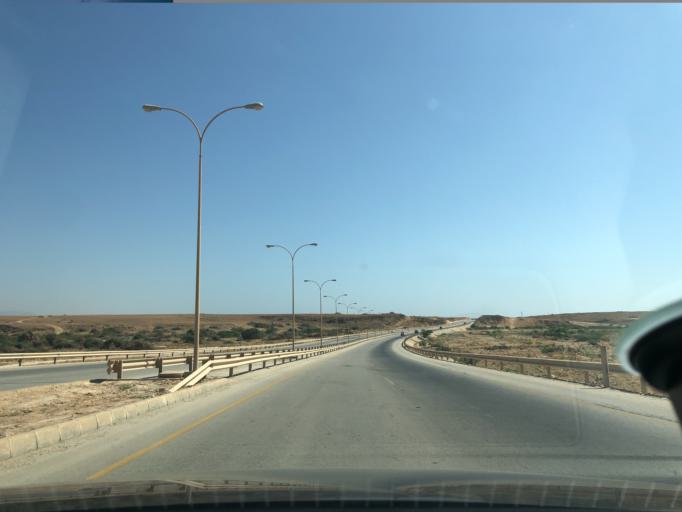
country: OM
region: Zufar
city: Salalah
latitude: 17.0499
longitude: 54.3288
